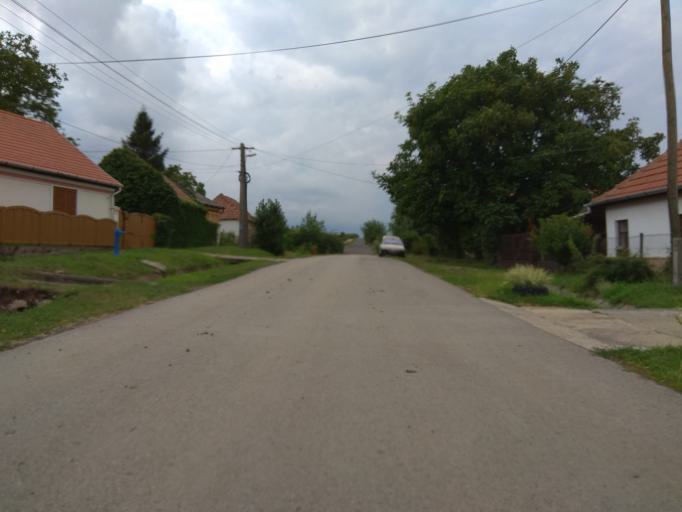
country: HU
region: Borsod-Abauj-Zemplen
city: Monok
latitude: 48.2086
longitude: 21.1422
